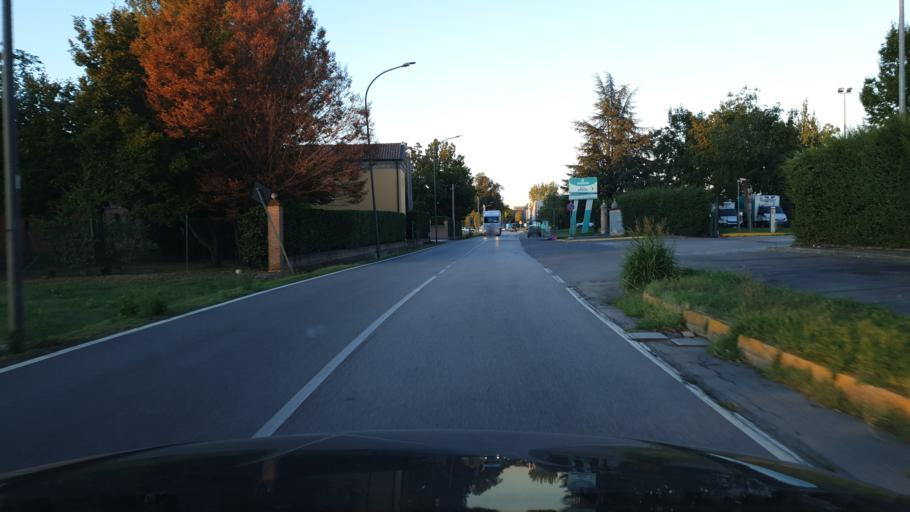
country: IT
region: Emilia-Romagna
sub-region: Provincia di Bologna
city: Quarto Inferiore
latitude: 44.5301
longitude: 11.3850
